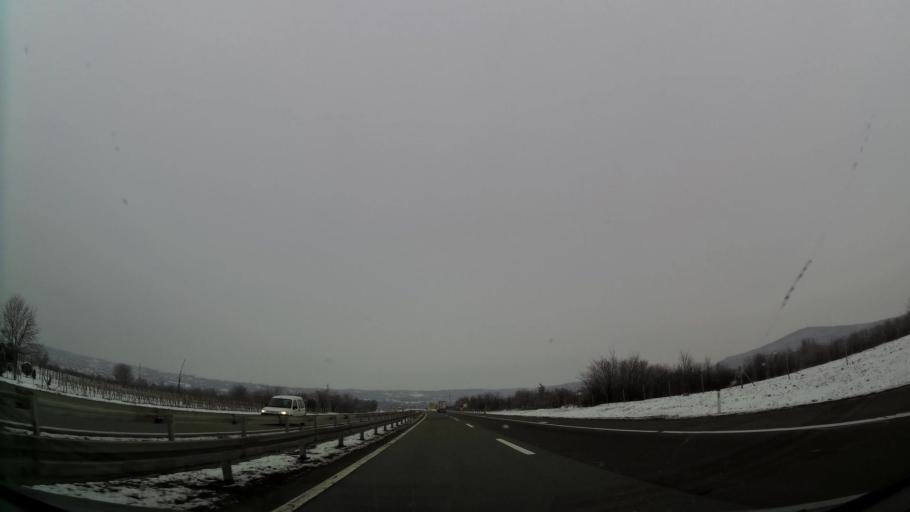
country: RS
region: Central Serbia
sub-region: Pomoravski Okrug
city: Paracin
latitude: 43.8489
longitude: 21.4328
